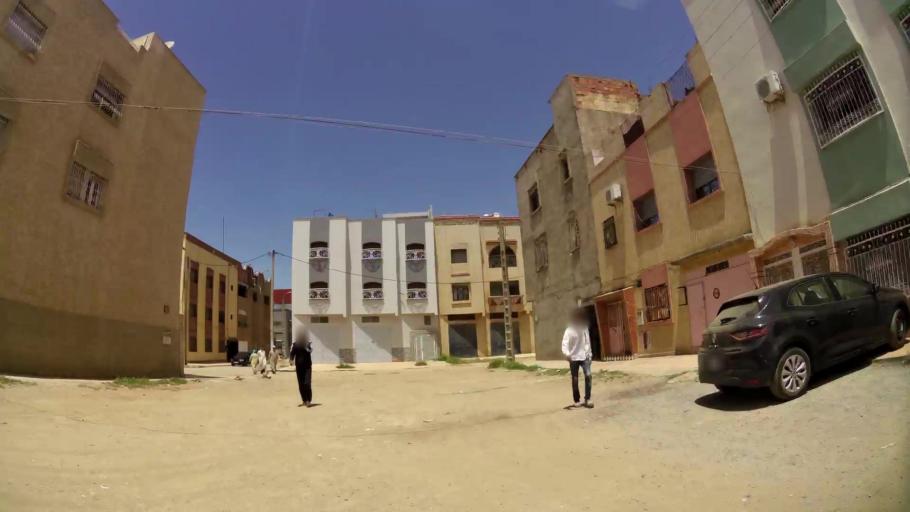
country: MA
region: Rabat-Sale-Zemmour-Zaer
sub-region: Khemisset
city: Khemisset
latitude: 33.8251
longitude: -6.0795
